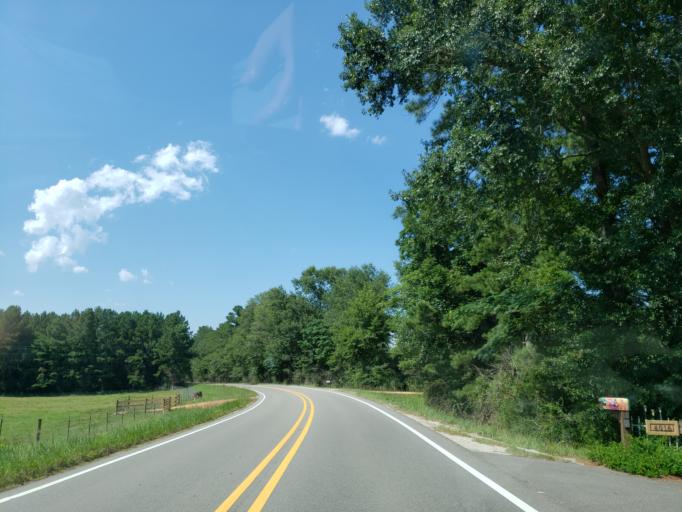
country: US
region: Mississippi
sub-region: Lamar County
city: Sumrall
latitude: 31.3705
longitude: -89.5090
